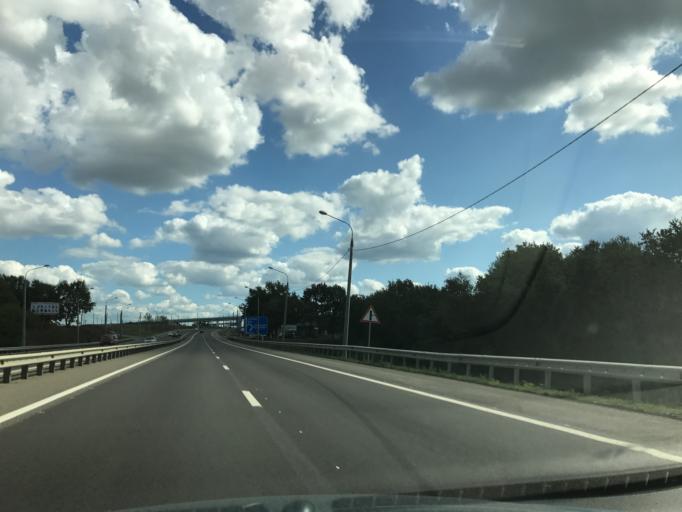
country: RU
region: Adygeya
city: Adygeysk
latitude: 44.8312
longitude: 39.2205
